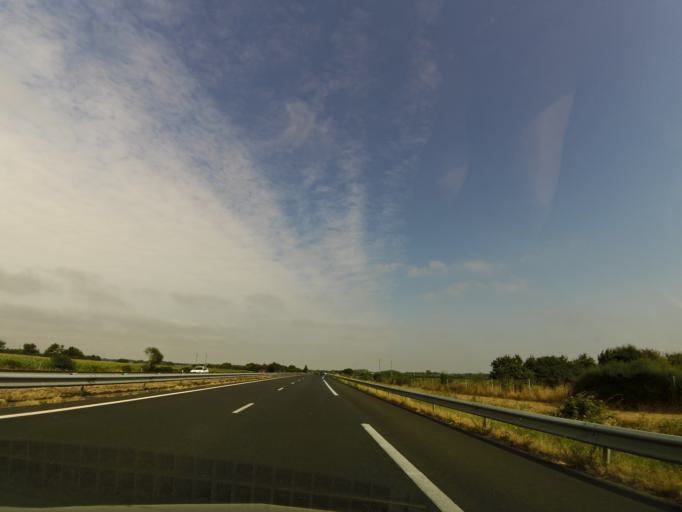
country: FR
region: Pays de la Loire
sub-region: Departement de la Vendee
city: Chauche
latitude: 46.8529
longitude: -1.2763
